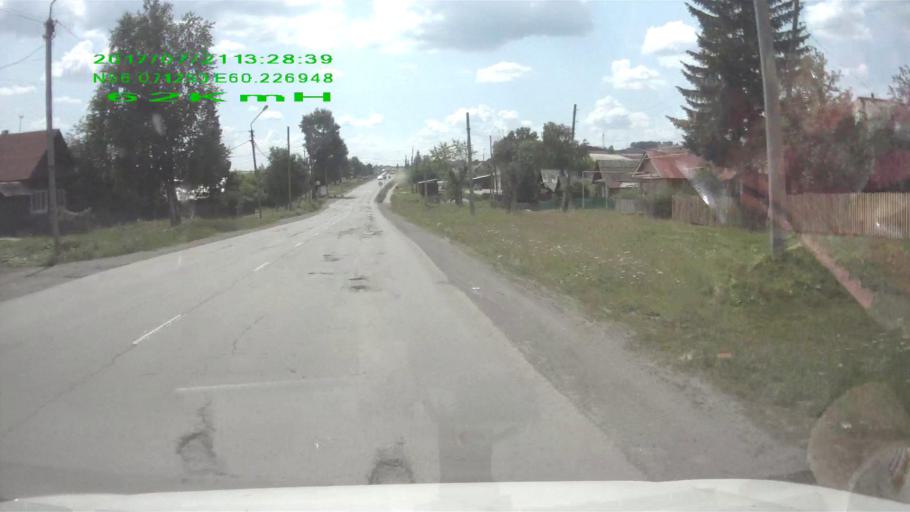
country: RU
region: Chelyabinsk
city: Verkhniy Ufaley
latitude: 56.0705
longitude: 60.2262
